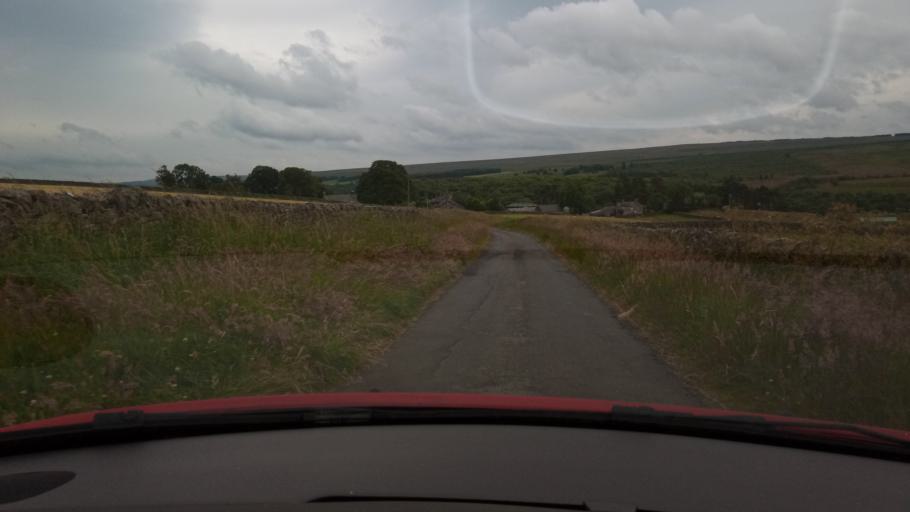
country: GB
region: England
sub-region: Northumberland
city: Rochester
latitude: 55.2800
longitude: -2.2650
